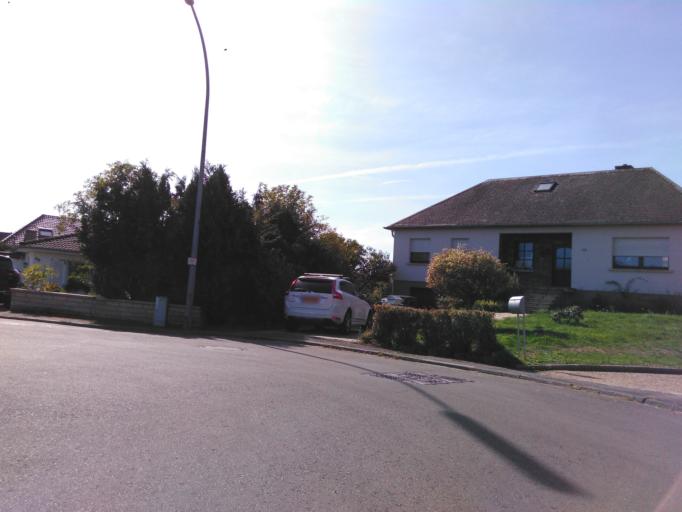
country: LU
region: Luxembourg
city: Bergem
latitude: 49.5068
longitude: 6.0472
